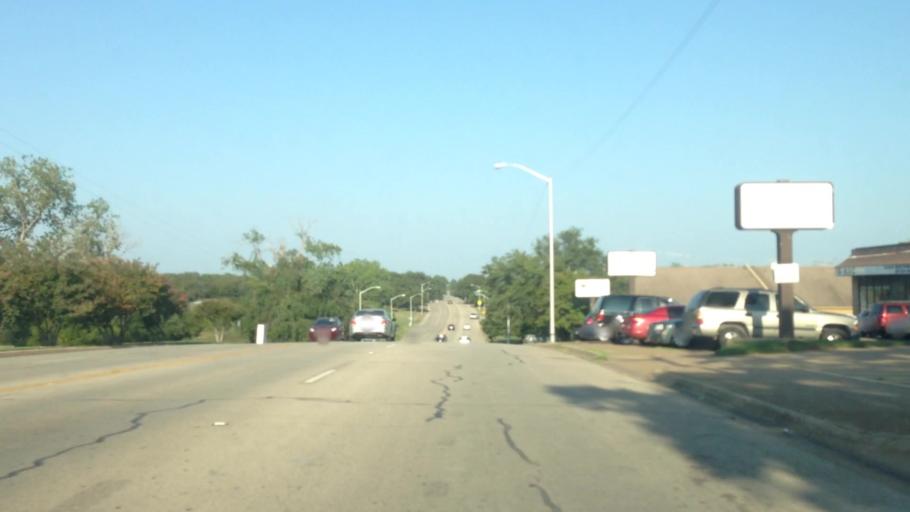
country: US
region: Texas
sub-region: Tarrant County
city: Richland Hills
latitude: 32.7543
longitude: -97.2138
